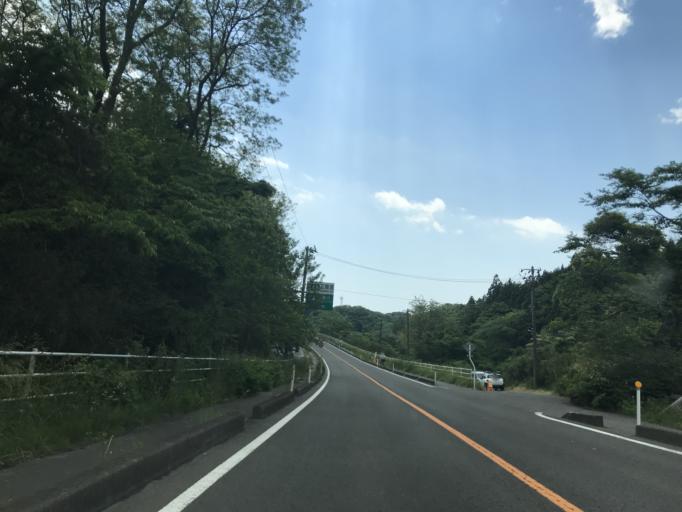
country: JP
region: Miyagi
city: Matsushima
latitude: 38.4092
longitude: 141.0639
